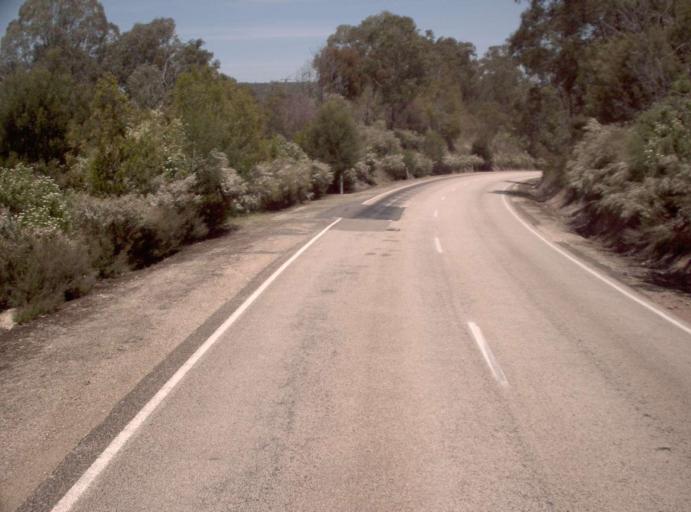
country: AU
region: Victoria
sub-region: East Gippsland
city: Lakes Entrance
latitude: -37.6615
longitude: 147.8774
